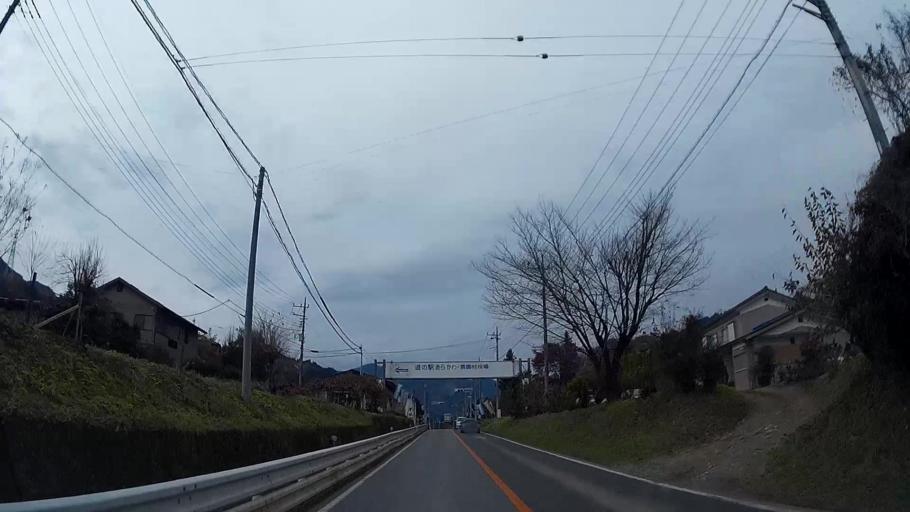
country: JP
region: Saitama
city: Chichibu
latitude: 35.9565
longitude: 139.0145
